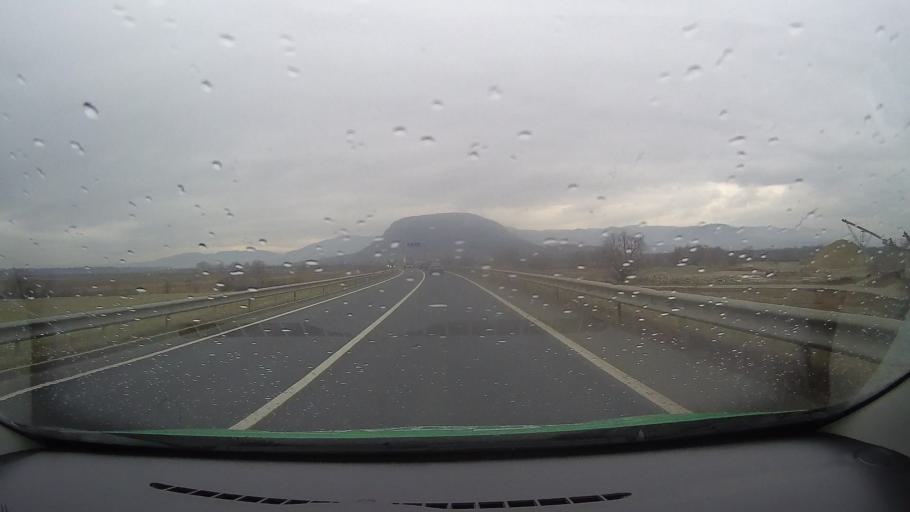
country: RO
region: Hunedoara
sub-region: Oras Simeria
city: Simeria
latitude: 45.8423
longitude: 23.0451
